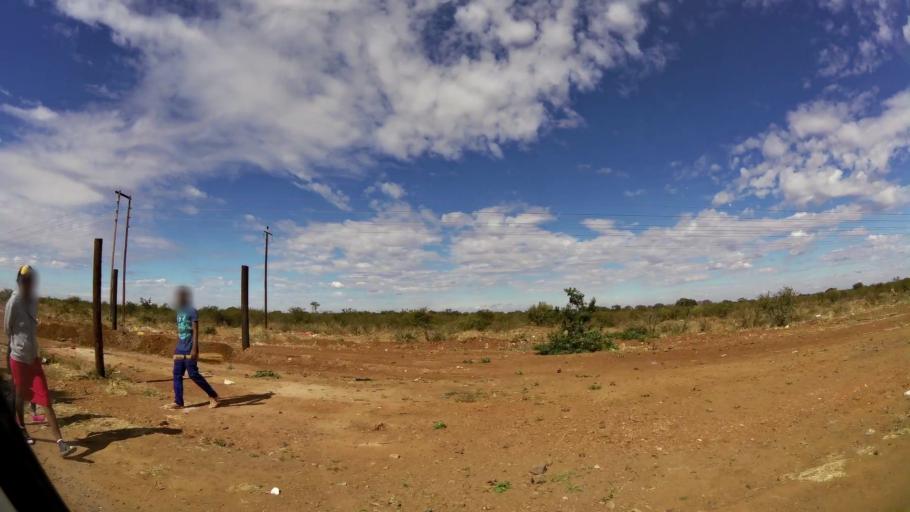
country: ZA
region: Limpopo
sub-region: Waterberg District Municipality
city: Bela-Bela
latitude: -24.8920
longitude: 28.3189
